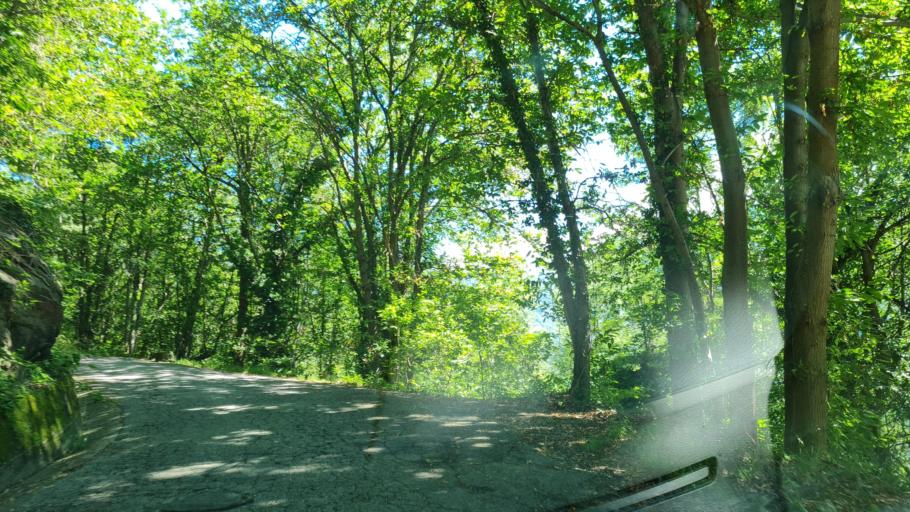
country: IT
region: Piedmont
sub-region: Provincia di Torino
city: Quincinetto
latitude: 45.5542
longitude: 7.8009
